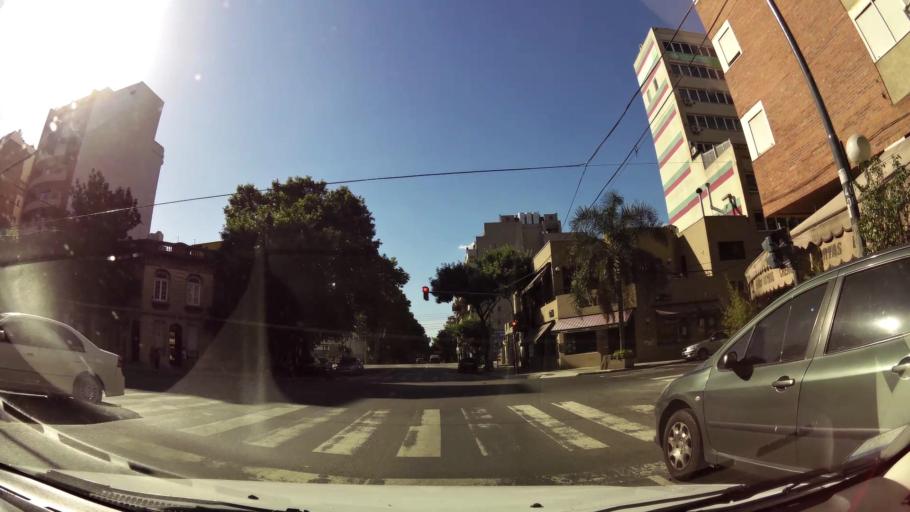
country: AR
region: Buenos Aires F.D.
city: Villa Santa Rita
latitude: -34.6258
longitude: -58.4573
